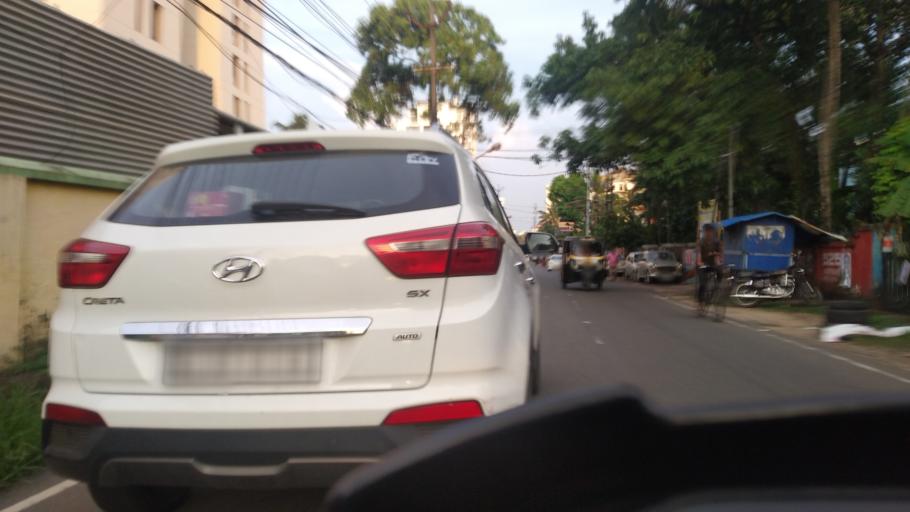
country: IN
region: Kerala
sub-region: Ernakulam
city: Elur
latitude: 10.0193
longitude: 76.2923
